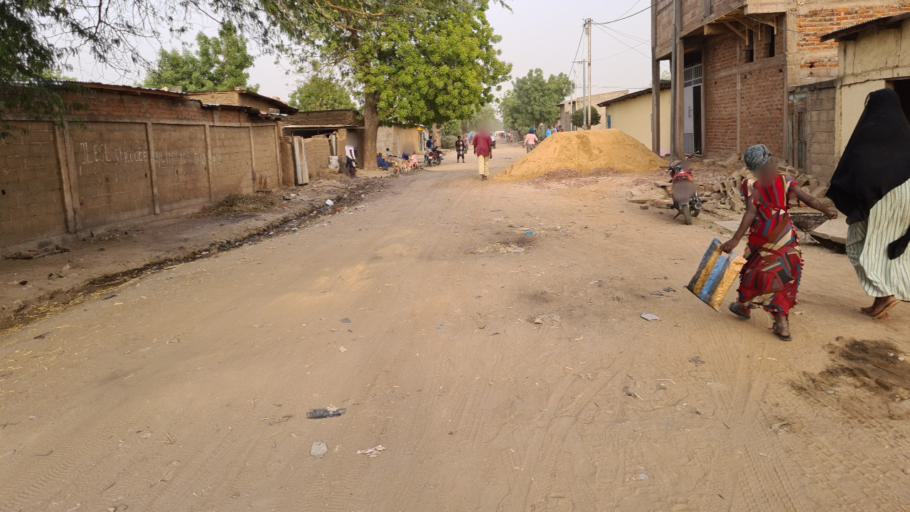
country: TD
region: Chari-Baguirmi
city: N'Djamena
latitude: 12.1044
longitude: 15.0744
